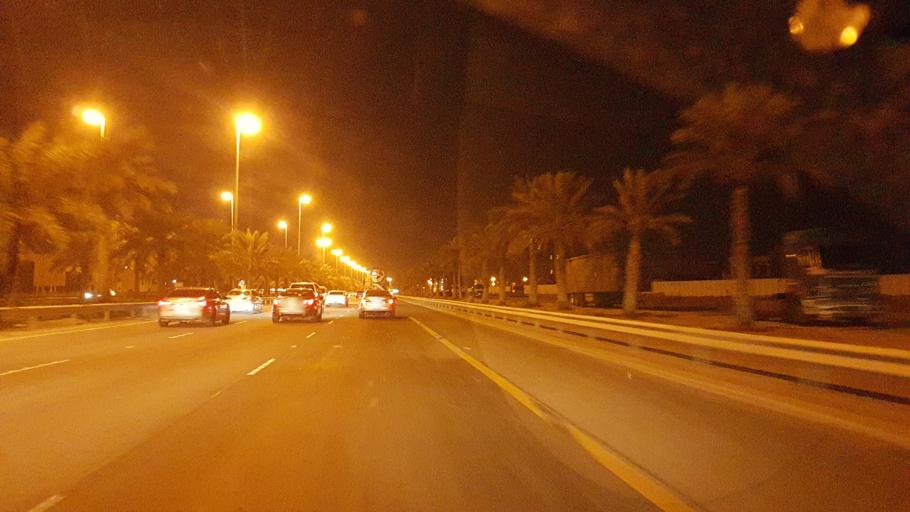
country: BH
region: Muharraq
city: Al Hadd
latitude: 26.2360
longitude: 50.6579
